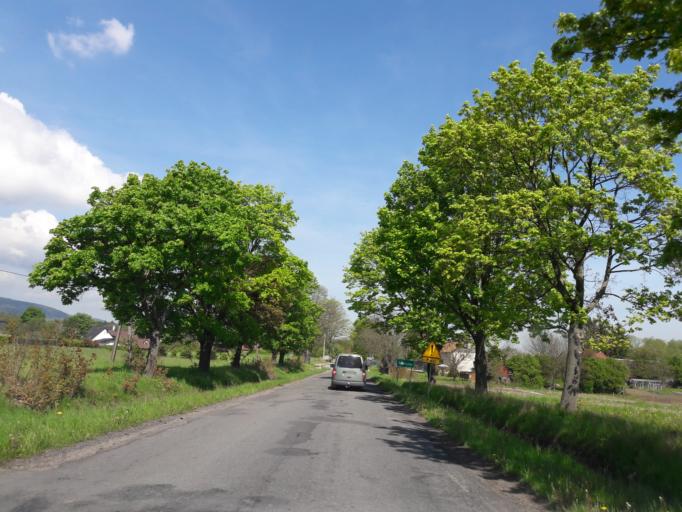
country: PL
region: Lower Silesian Voivodeship
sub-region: Powiat klodzki
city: Bystrzyca Klodzka
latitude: 50.3289
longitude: 16.6044
